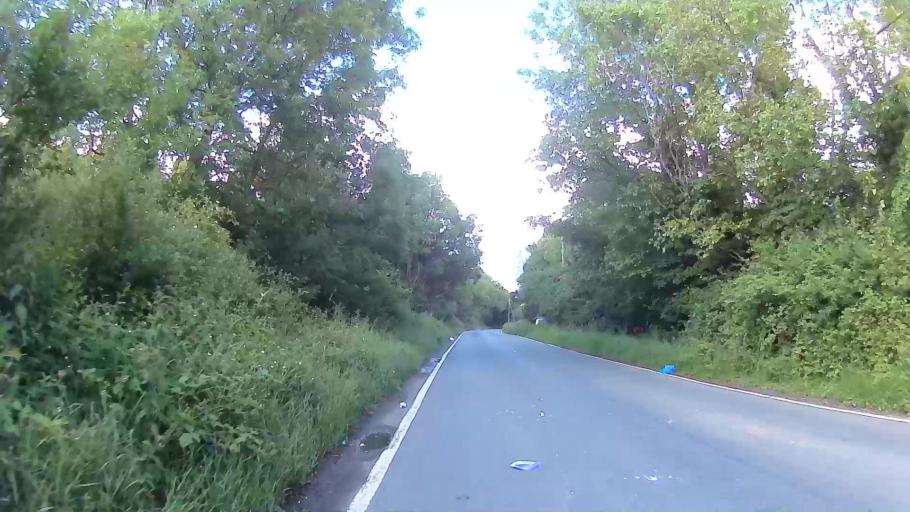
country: GB
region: England
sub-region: Greater London
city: Harold Wood
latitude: 51.6355
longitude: 0.2136
